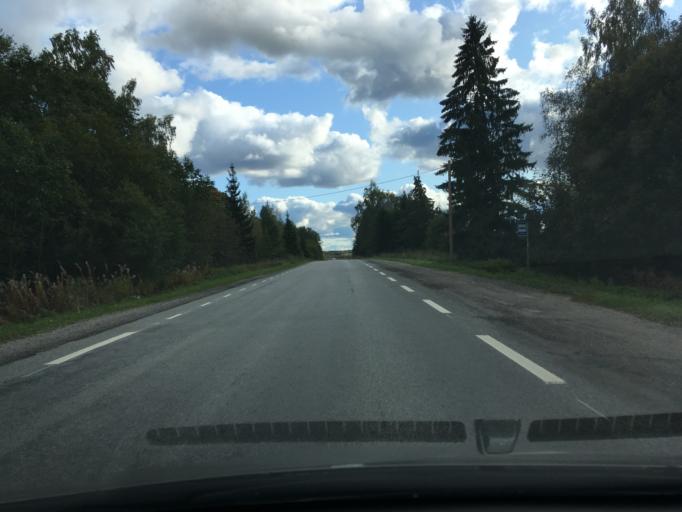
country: EE
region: Harju
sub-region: Raasiku vald
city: Raasiku
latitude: 59.3181
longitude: 25.1588
